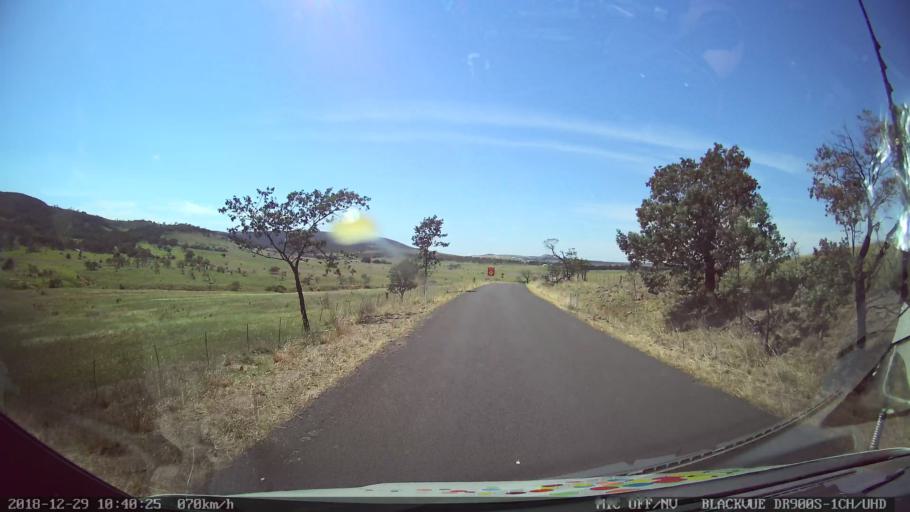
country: AU
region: New South Wales
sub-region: Palerang
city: Bungendore
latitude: -35.0151
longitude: 149.5184
